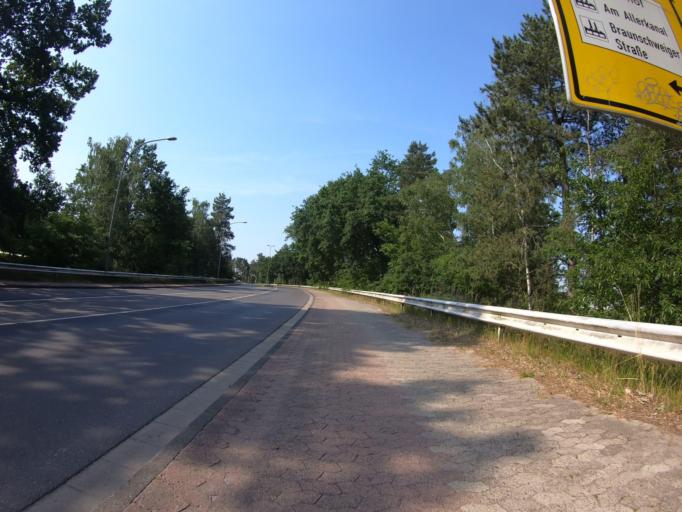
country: DE
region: Lower Saxony
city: Gifhorn
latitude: 52.4709
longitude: 10.5308
